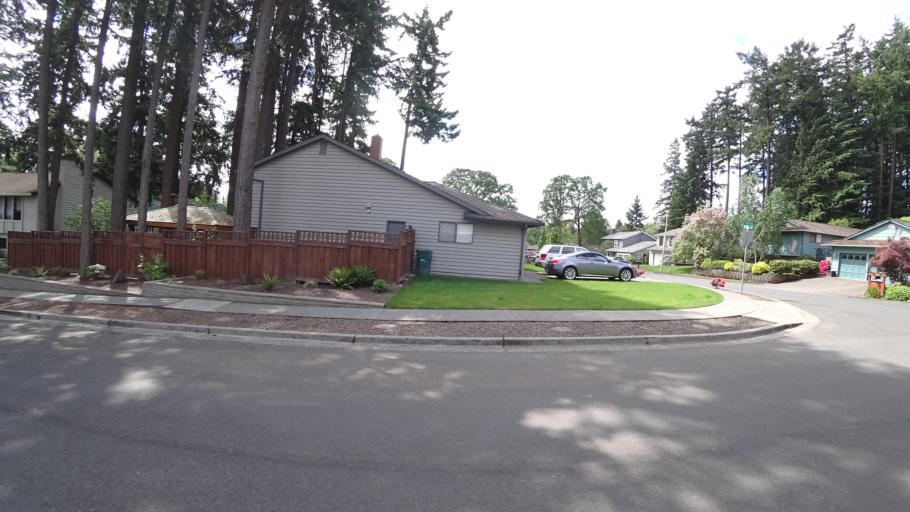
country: US
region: Oregon
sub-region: Washington County
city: Beaverton
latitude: 45.4701
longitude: -122.8083
